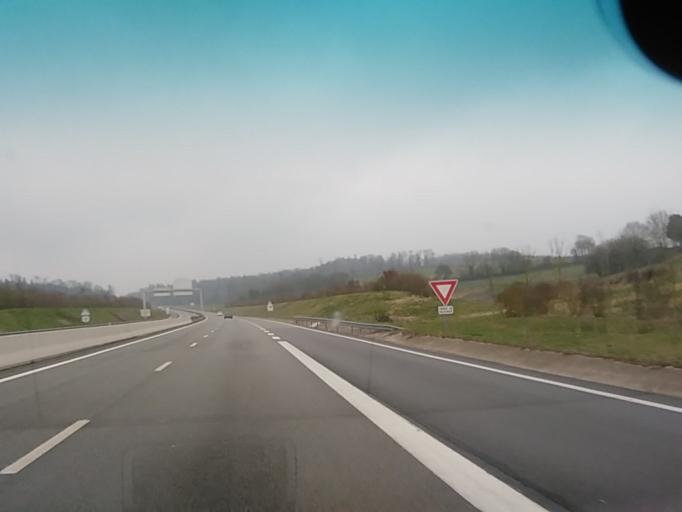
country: FR
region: Lower Normandy
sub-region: Departement de l'Orne
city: Gace
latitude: 48.7746
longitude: 0.3072
